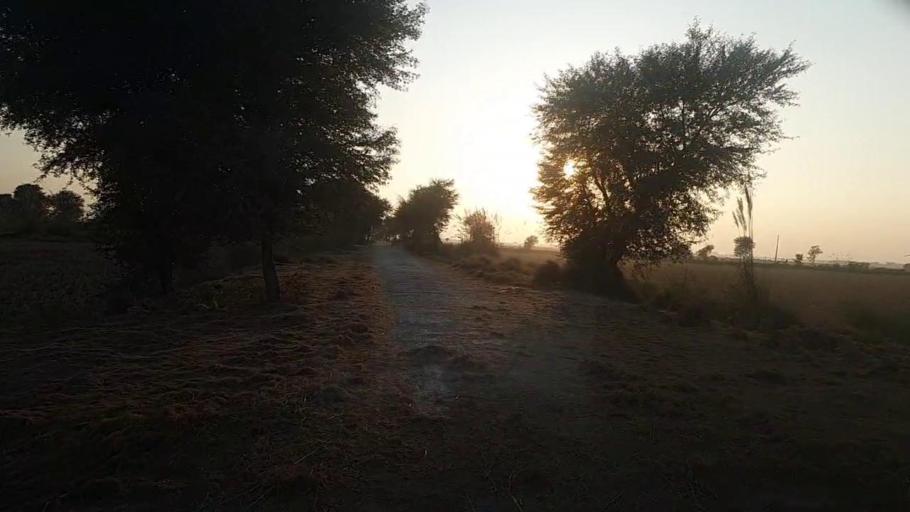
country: PK
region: Sindh
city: Mehar
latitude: 27.1819
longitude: 67.7355
